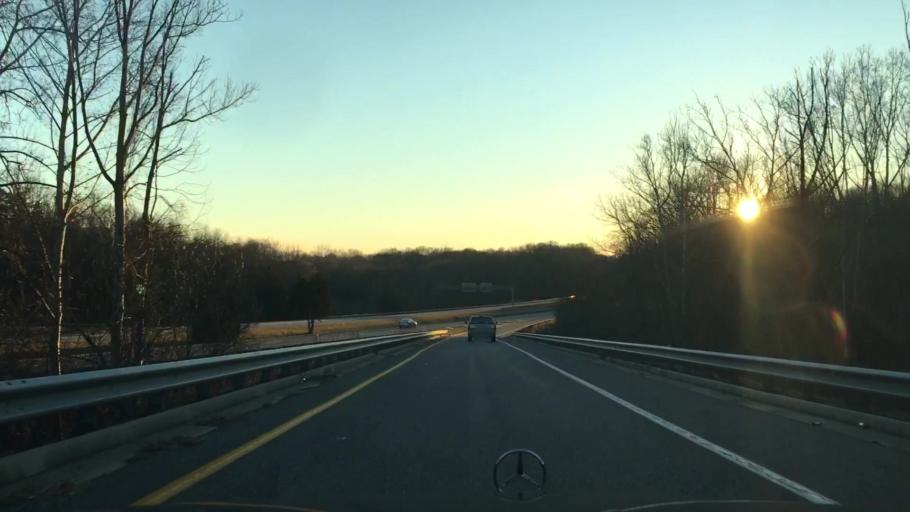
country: US
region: Virginia
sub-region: Campbell County
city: Altavista
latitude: 37.1279
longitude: -79.3092
